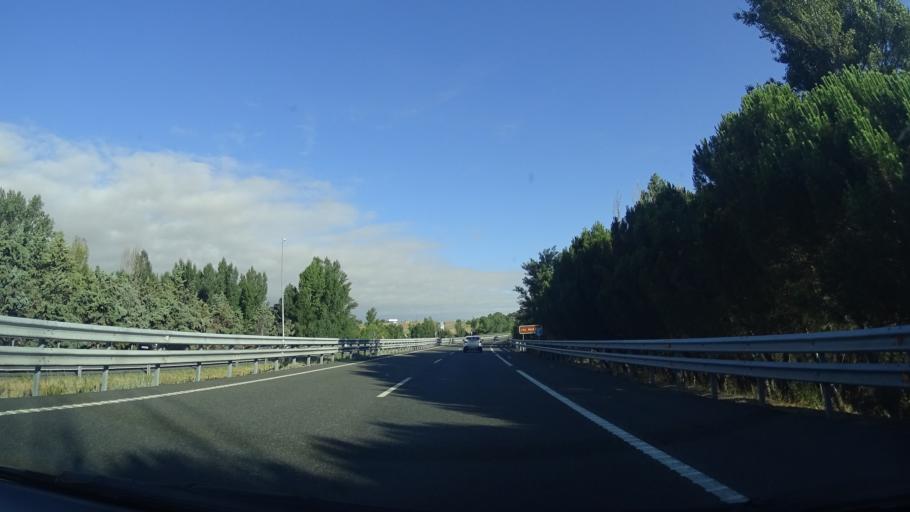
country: ES
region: Castille and Leon
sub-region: Provincia de Avila
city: Sanchidrian
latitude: 40.8641
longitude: -4.5627
